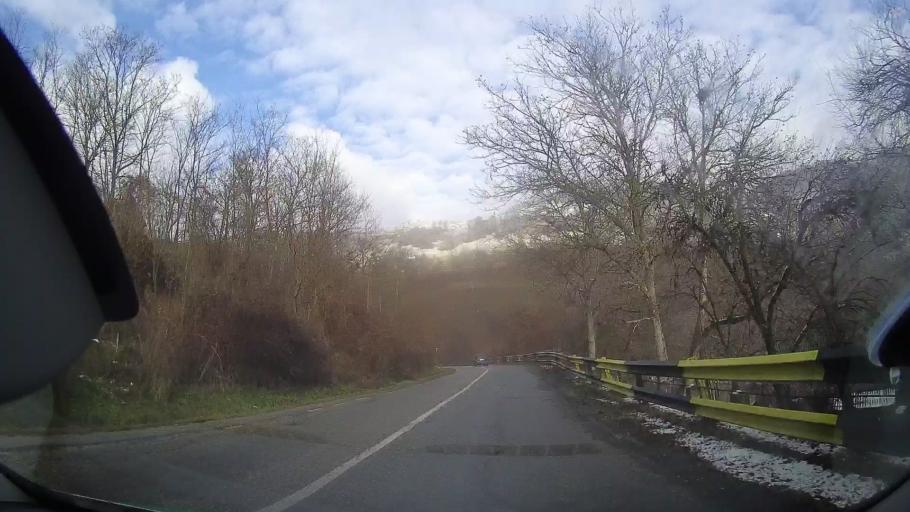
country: RO
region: Alba
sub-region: Comuna Lupsa
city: Lupsa
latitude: 46.3822
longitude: 23.2302
